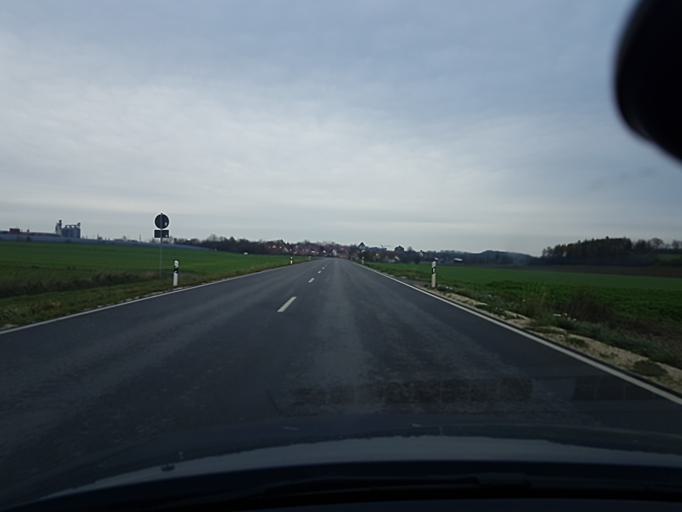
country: DE
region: Bavaria
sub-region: Upper Palatinate
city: Schierling
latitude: 48.8285
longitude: 12.1782
